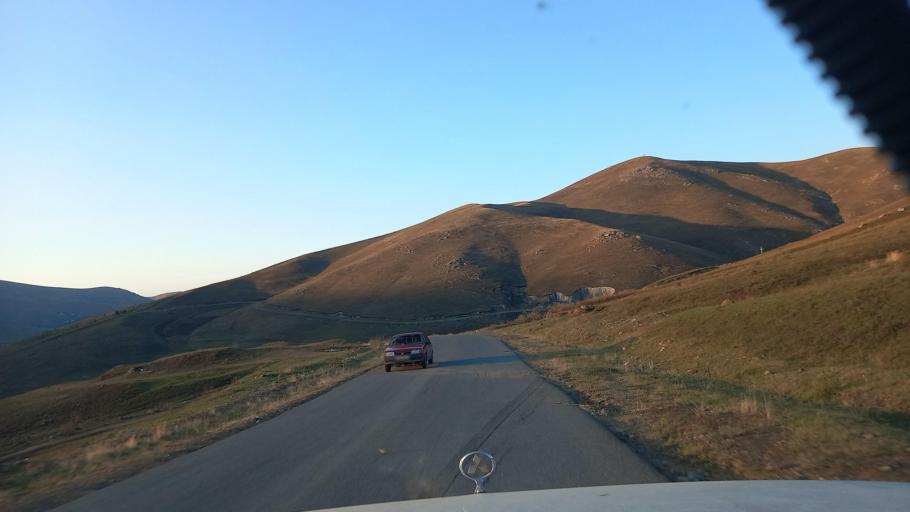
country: AZ
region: Gadabay Rayon
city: Ariqdam
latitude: 40.6825
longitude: 45.7720
